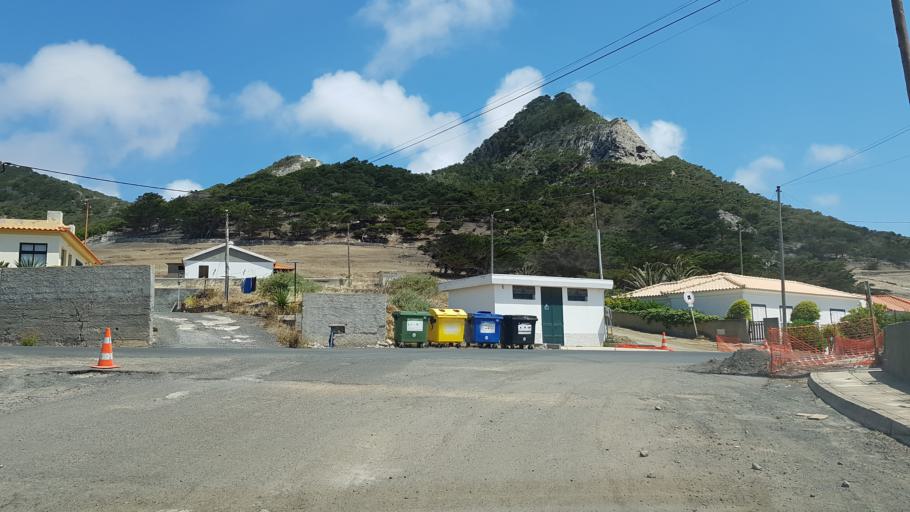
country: PT
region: Madeira
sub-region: Porto Santo
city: Camacha
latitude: 33.0866
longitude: -16.3385
